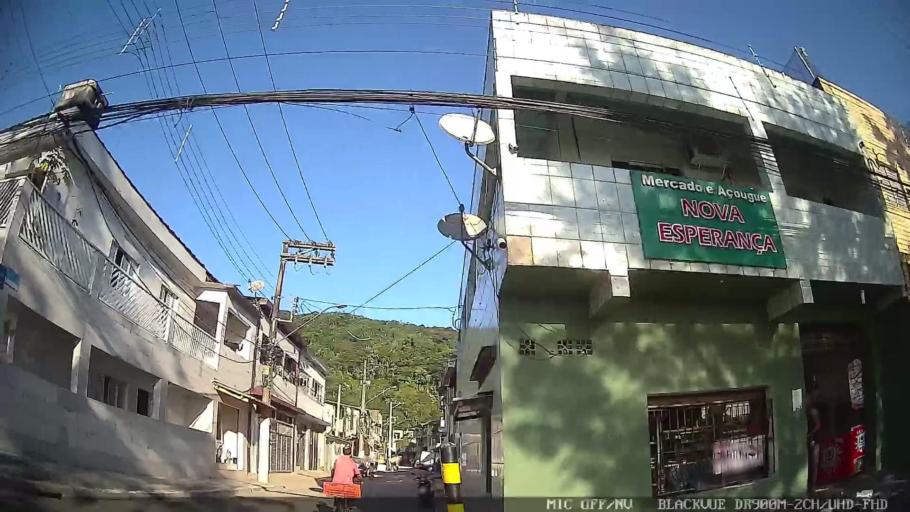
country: BR
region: Sao Paulo
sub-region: Guaruja
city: Guaruja
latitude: -23.9715
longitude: -46.2490
